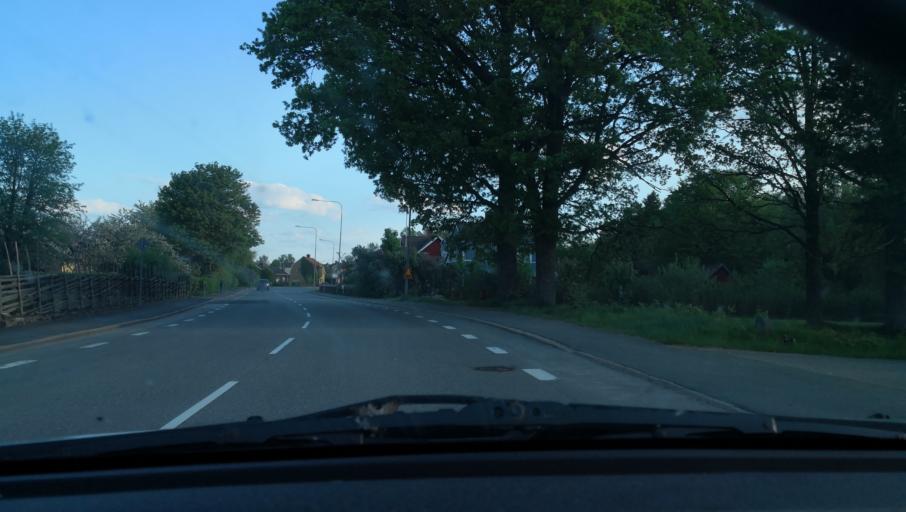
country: SE
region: Joenkoeping
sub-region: Nassjo Kommun
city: Bodafors
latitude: 57.5017
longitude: 14.7096
